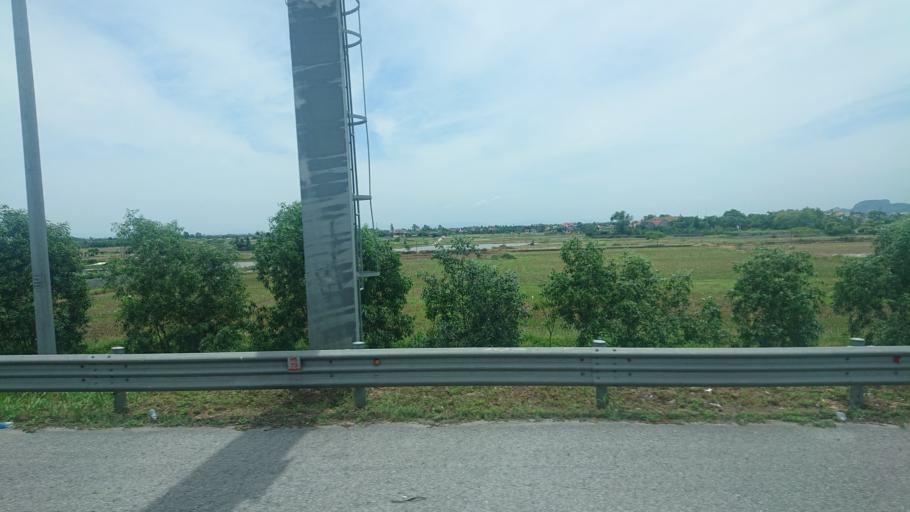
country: VN
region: Hai Phong
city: An Lao
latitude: 20.8057
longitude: 106.5184
